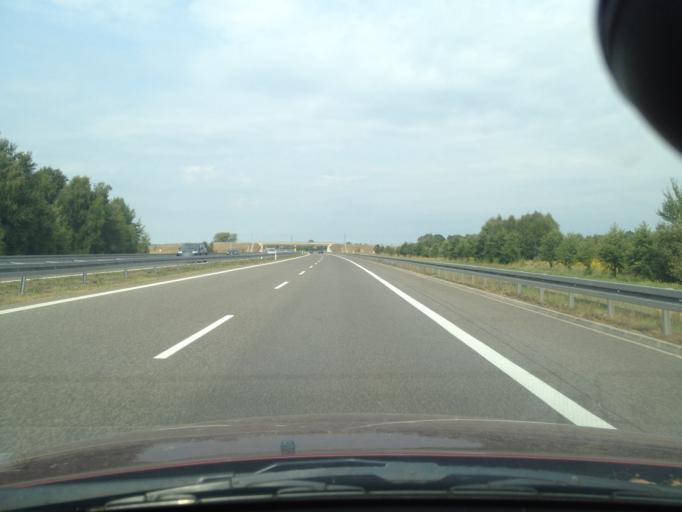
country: PL
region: West Pomeranian Voivodeship
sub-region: Powiat mysliborski
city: Nowogrodek Pomorski
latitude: 52.9383
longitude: 14.9774
